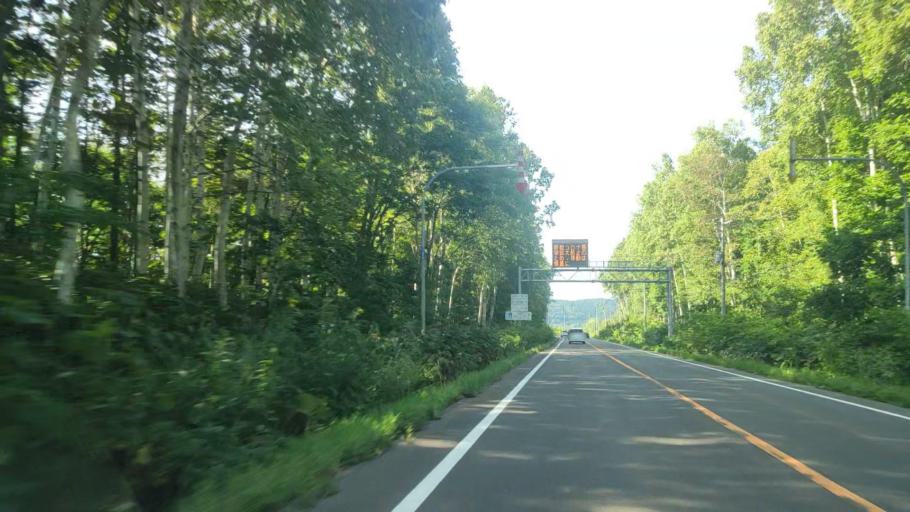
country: JP
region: Hokkaido
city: Nayoro
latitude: 44.7165
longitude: 142.2720
